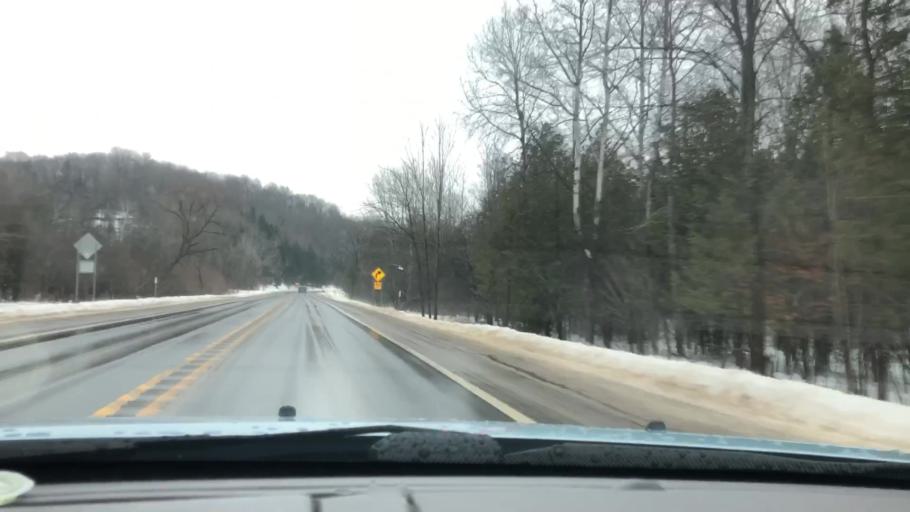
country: US
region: Michigan
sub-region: Charlevoix County
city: East Jordan
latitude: 45.1286
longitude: -85.0776
